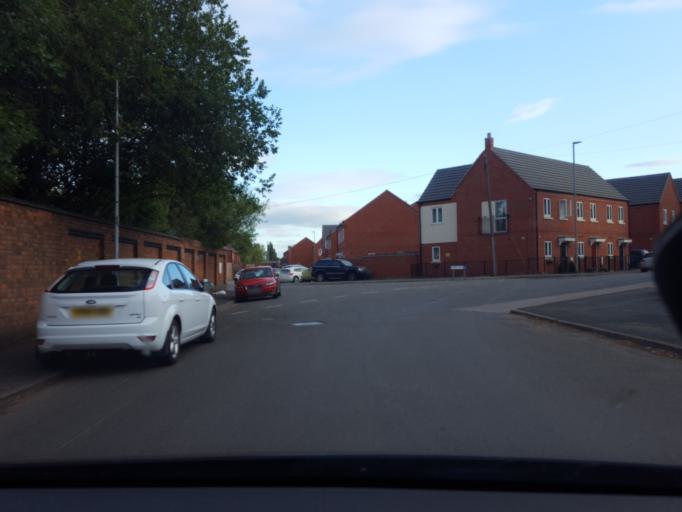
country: GB
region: England
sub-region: Leicestershire
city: Loughborough
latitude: 52.7696
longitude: -1.1921
